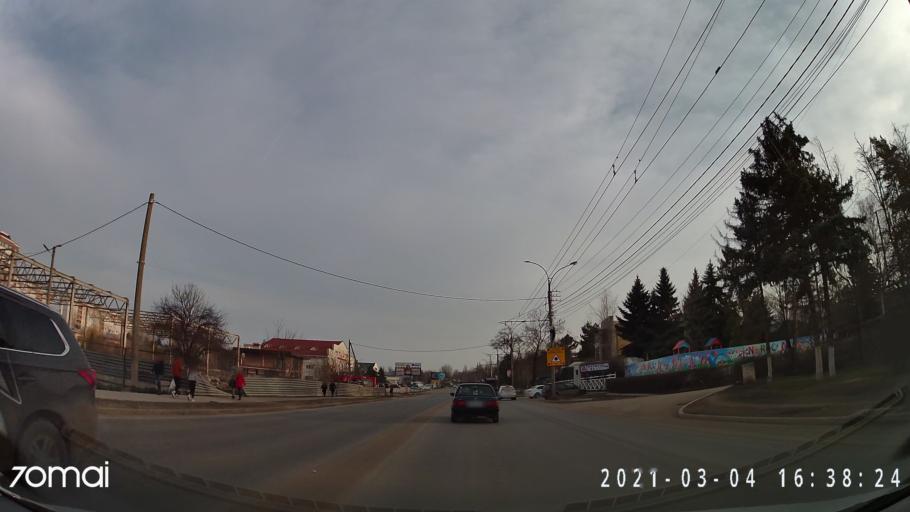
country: MD
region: Balti
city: Balti
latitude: 47.7812
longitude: 27.8908
